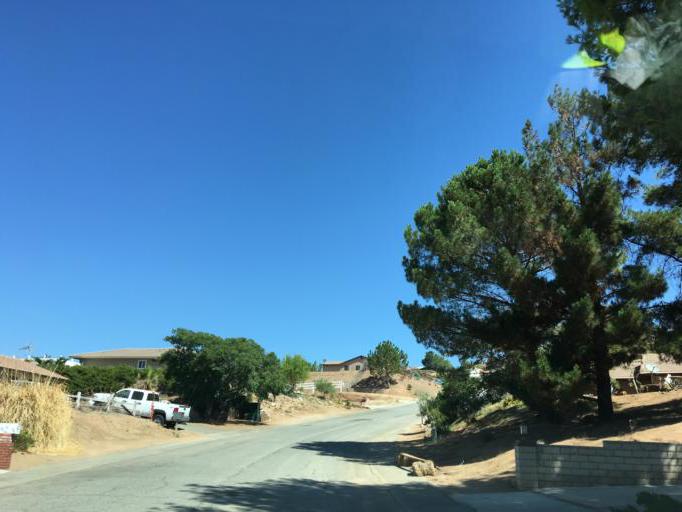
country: US
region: California
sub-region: Los Angeles County
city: Acton
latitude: 34.4936
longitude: -118.1618
